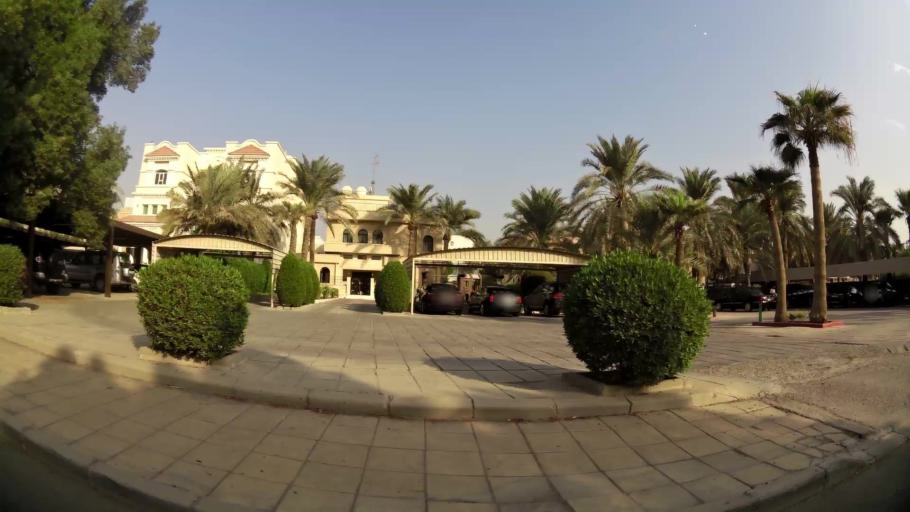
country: KW
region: Mubarak al Kabir
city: Sabah as Salim
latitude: 29.2733
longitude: 48.0702
